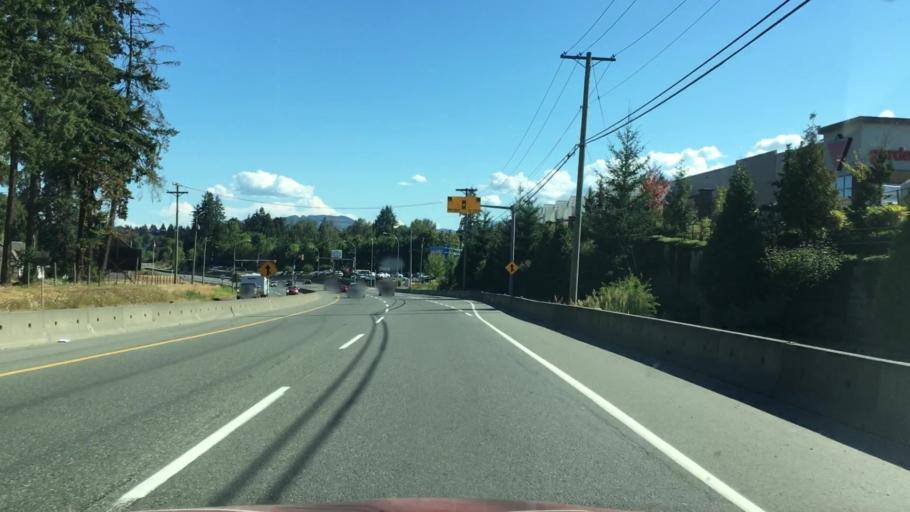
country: CA
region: British Columbia
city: Duncan
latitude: 48.8013
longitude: -123.7168
